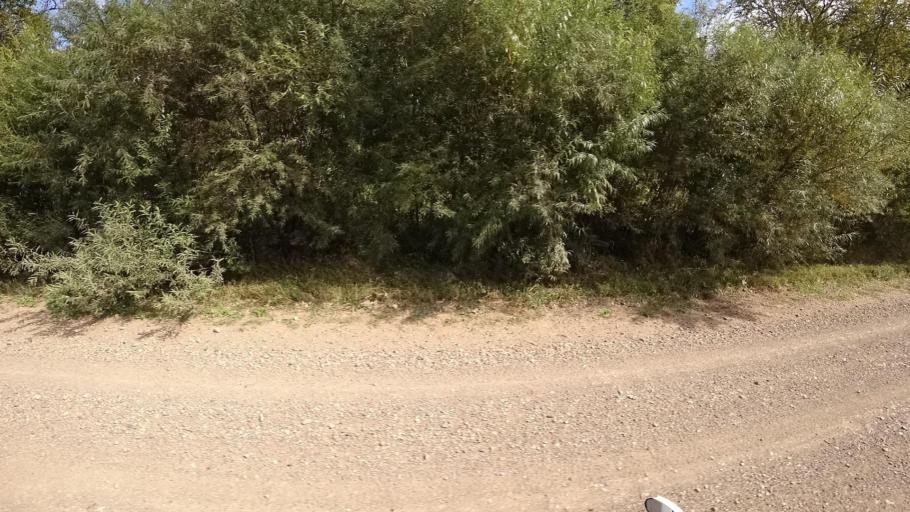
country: RU
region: Primorskiy
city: Yakovlevka
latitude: 44.7141
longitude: 133.6196
